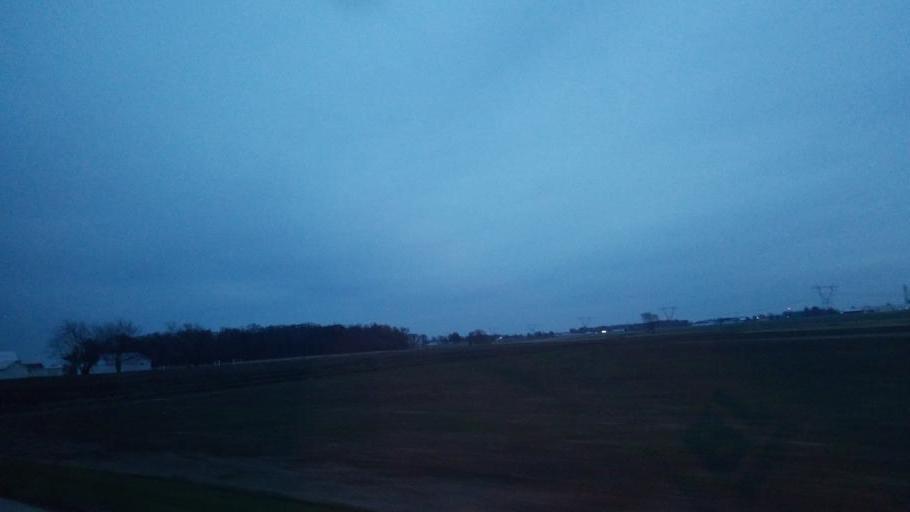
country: US
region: Indiana
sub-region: Adams County
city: Berne
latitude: 40.7158
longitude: -84.9709
